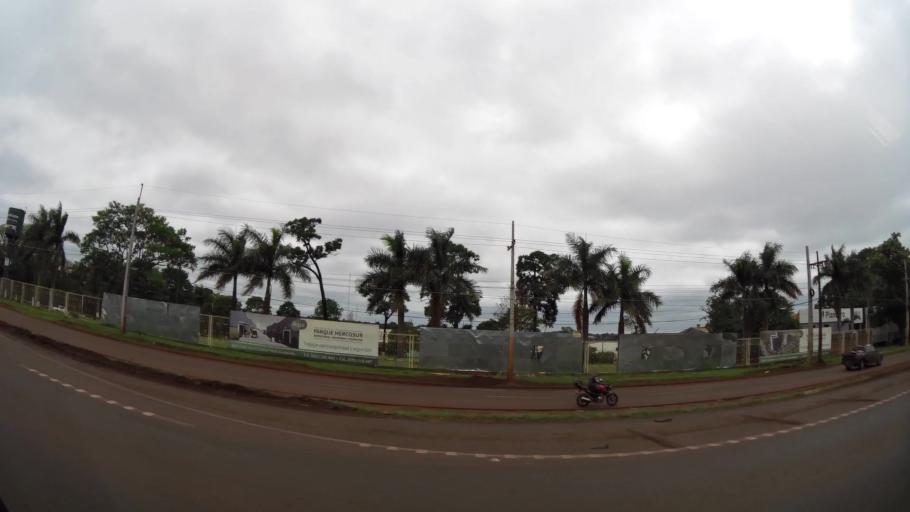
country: PY
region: Alto Parana
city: Ciudad del Este
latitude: -25.4955
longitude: -54.6938
